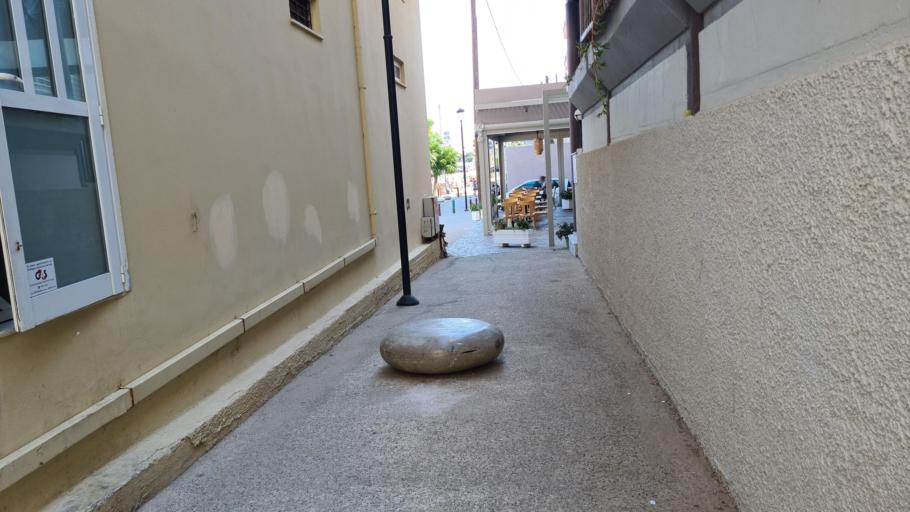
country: GR
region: Crete
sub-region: Nomos Chanias
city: Chania
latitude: 35.5131
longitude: 24.0059
